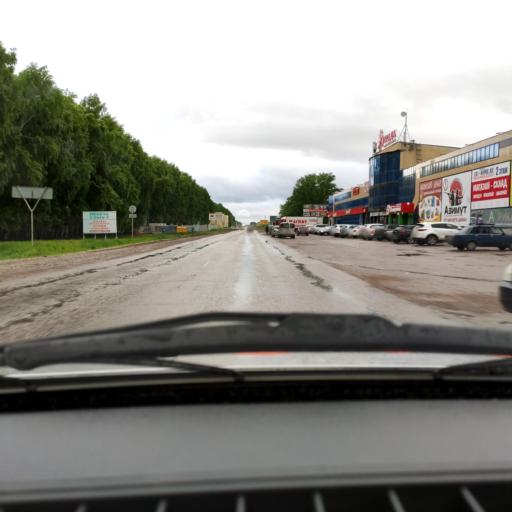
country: RU
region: Bashkortostan
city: Sterlitamak
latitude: 53.5882
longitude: 55.8966
